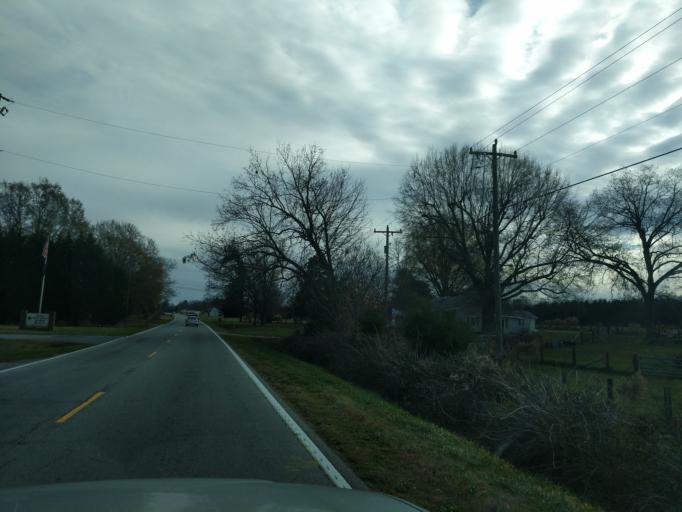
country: US
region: South Carolina
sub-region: Anderson County
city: Piedmont
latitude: 34.6966
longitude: -82.5561
